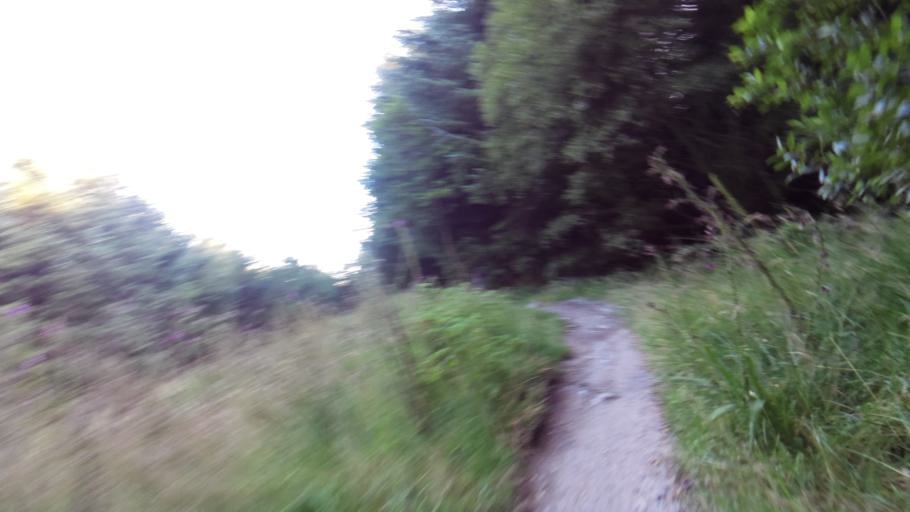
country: GB
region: England
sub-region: North Yorkshire
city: Settle
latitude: 54.0066
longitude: -2.3759
